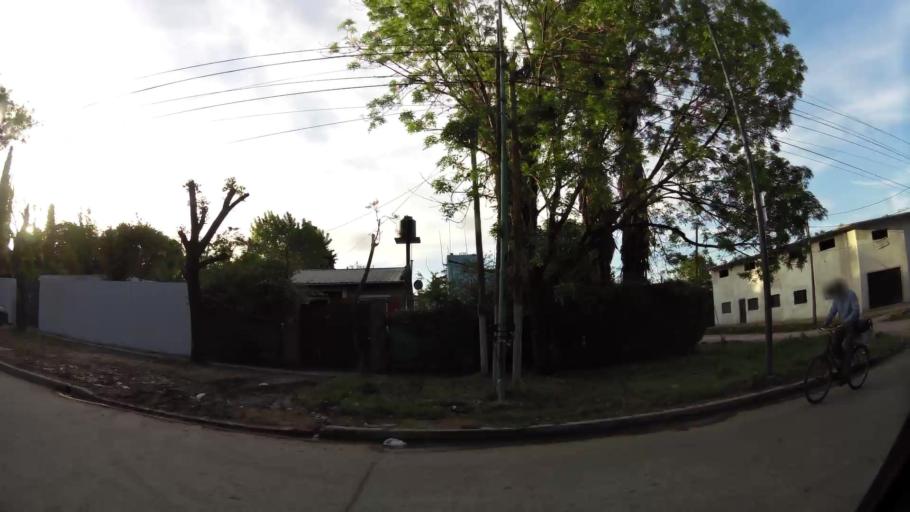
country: AR
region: Buenos Aires
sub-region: Partido de Quilmes
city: Quilmes
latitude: -34.7956
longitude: -58.1942
